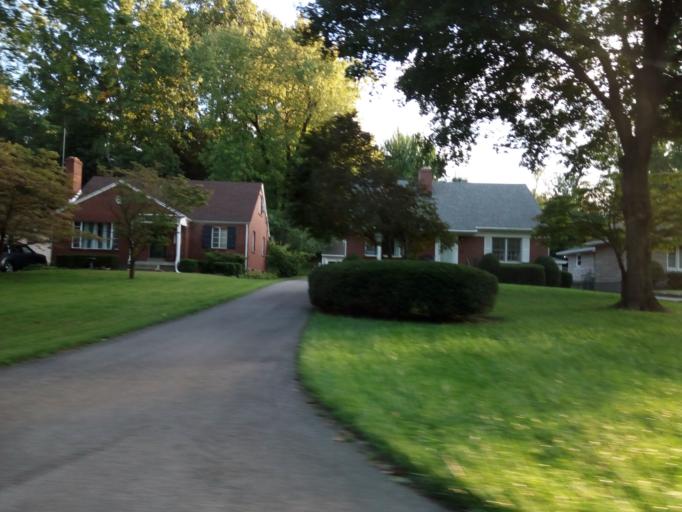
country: US
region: Kentucky
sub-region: Jefferson County
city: Audubon Park
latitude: 38.2049
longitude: -85.7225
